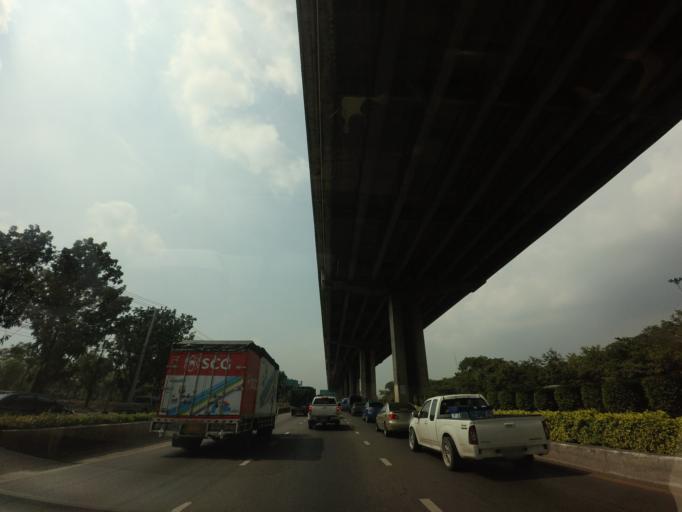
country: TH
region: Bangkok
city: Thawi Watthana
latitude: 13.7845
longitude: 100.3933
